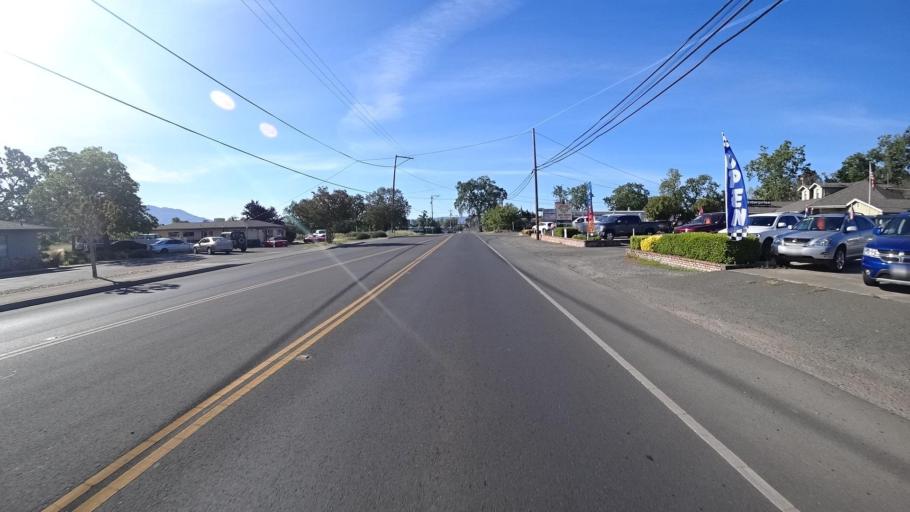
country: US
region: California
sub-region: Lake County
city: Lakeport
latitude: 39.0251
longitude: -122.9157
